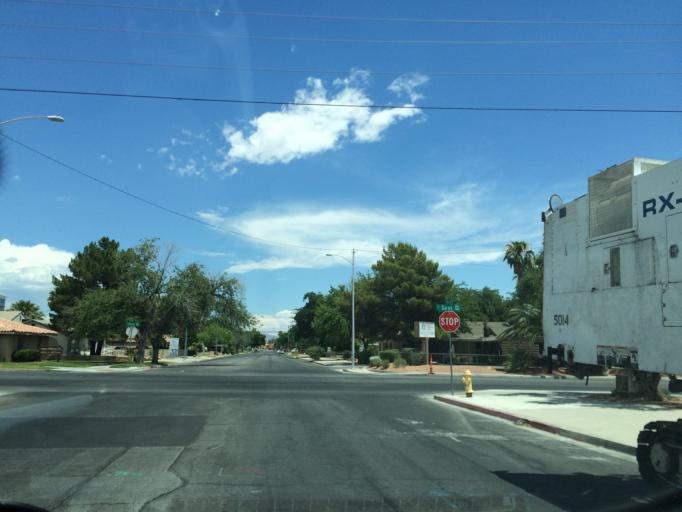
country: US
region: Nevada
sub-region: Clark County
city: Las Vegas
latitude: 36.1593
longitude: -115.1428
